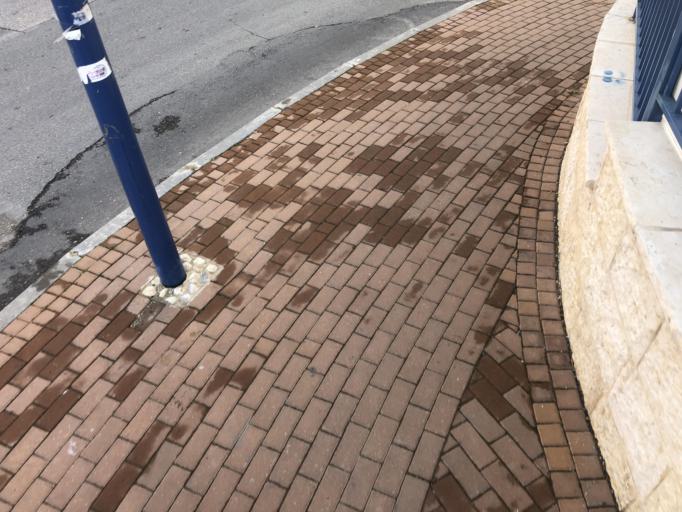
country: IL
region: Jerusalem
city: Modiin Ilit
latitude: 31.9225
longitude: 35.0540
